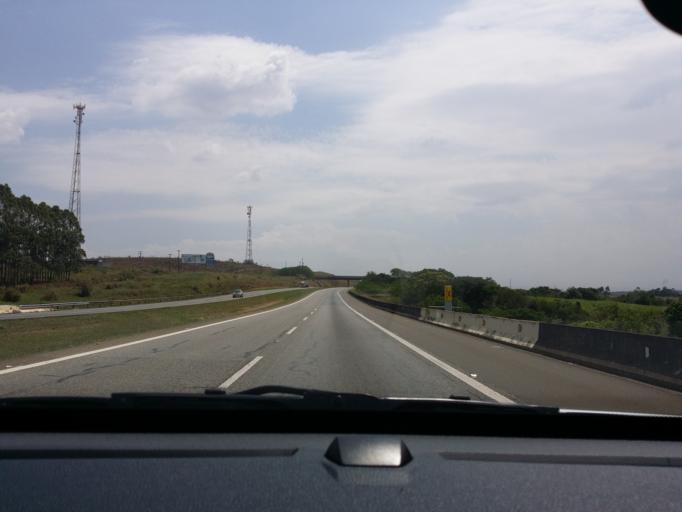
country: BR
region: Sao Paulo
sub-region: Santa Barbara D'Oeste
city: Santa Barbara d'Oeste
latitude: -22.6698
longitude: -47.4466
